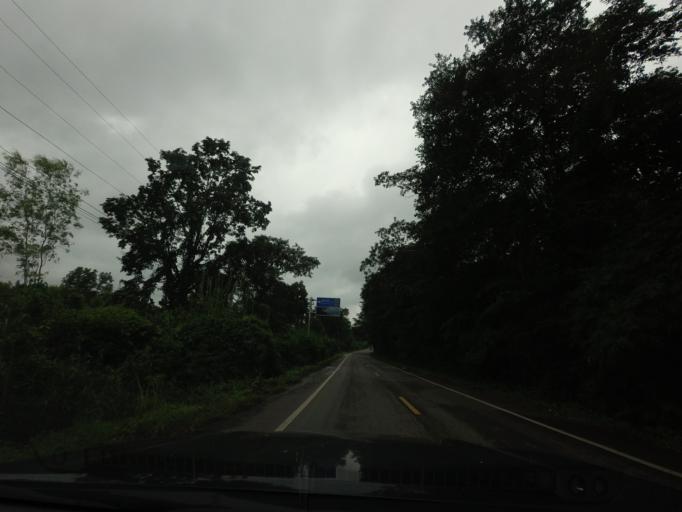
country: TH
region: Nong Khai
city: Sangkhom
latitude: 18.0261
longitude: 102.3556
